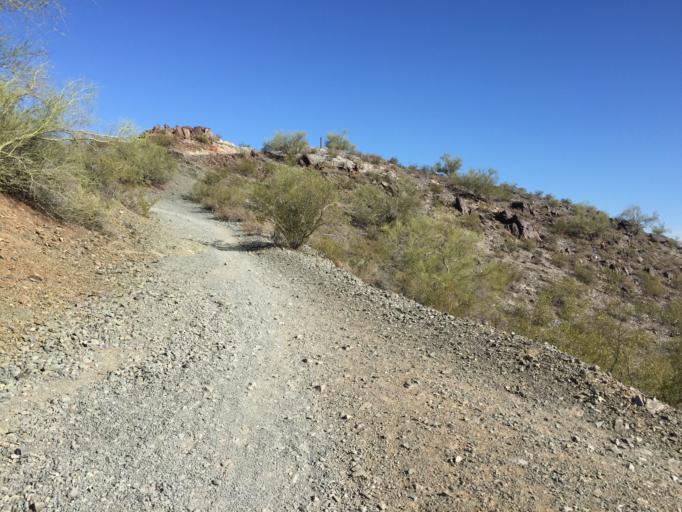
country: US
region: Arizona
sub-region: Maricopa County
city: Paradise Valley
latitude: 33.5610
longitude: -112.0216
